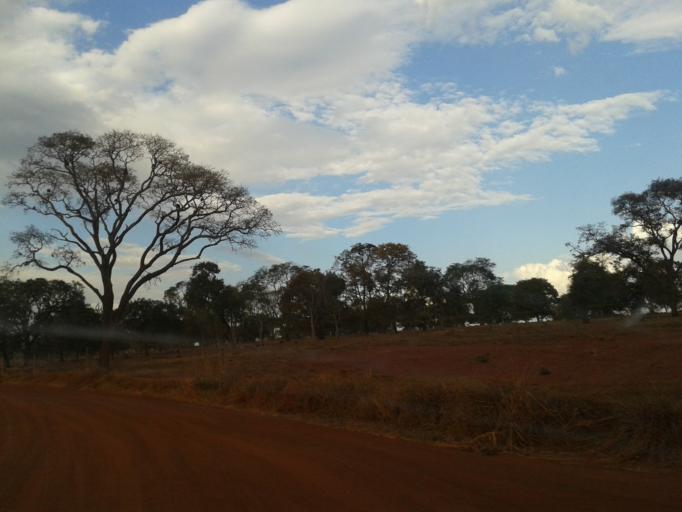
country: BR
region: Minas Gerais
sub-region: Ituiutaba
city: Ituiutaba
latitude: -19.1990
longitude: -49.8400
